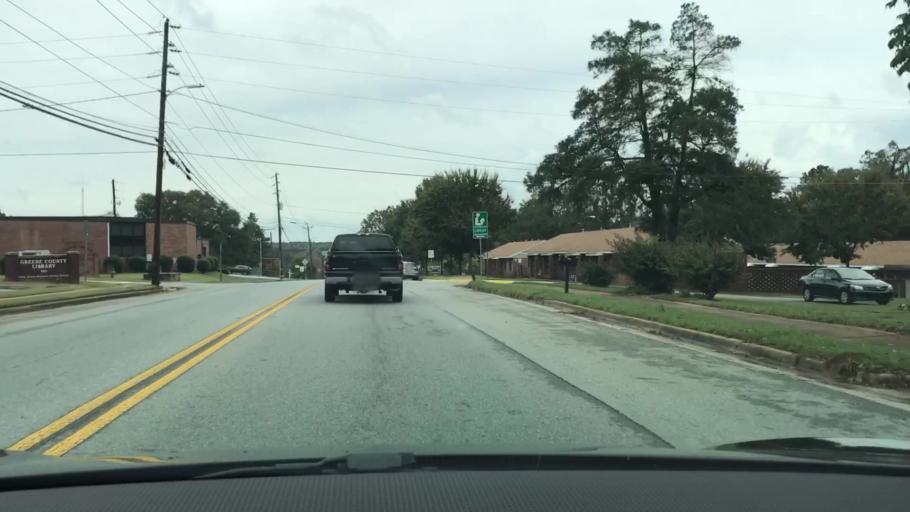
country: US
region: Georgia
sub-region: Greene County
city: Greensboro
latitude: 33.5688
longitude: -83.1834
